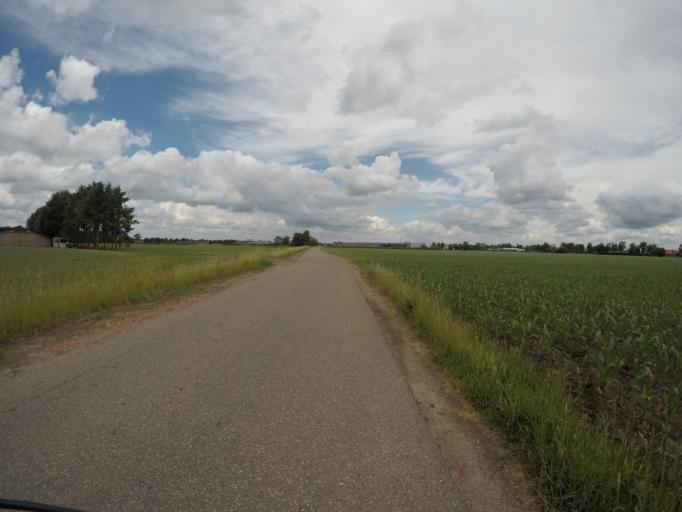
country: BE
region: Flanders
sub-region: Provincie Antwerpen
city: Rijkevorsel
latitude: 51.3729
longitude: 4.7502
